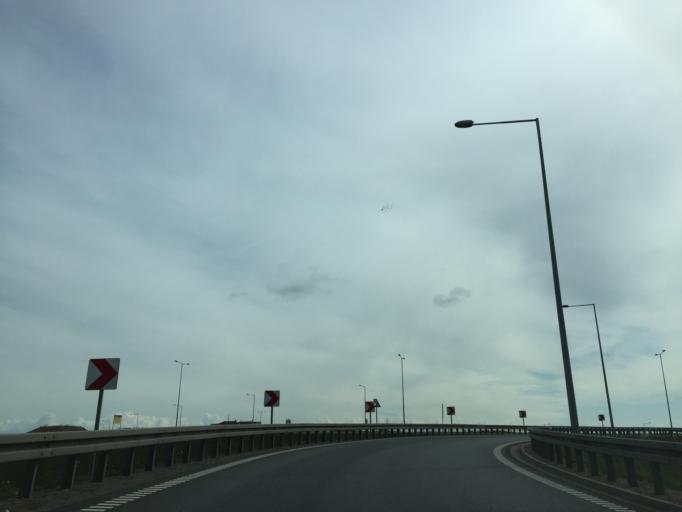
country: PL
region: Podlasie
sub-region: Suwalki
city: Suwalki
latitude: 54.0503
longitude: 22.8898
